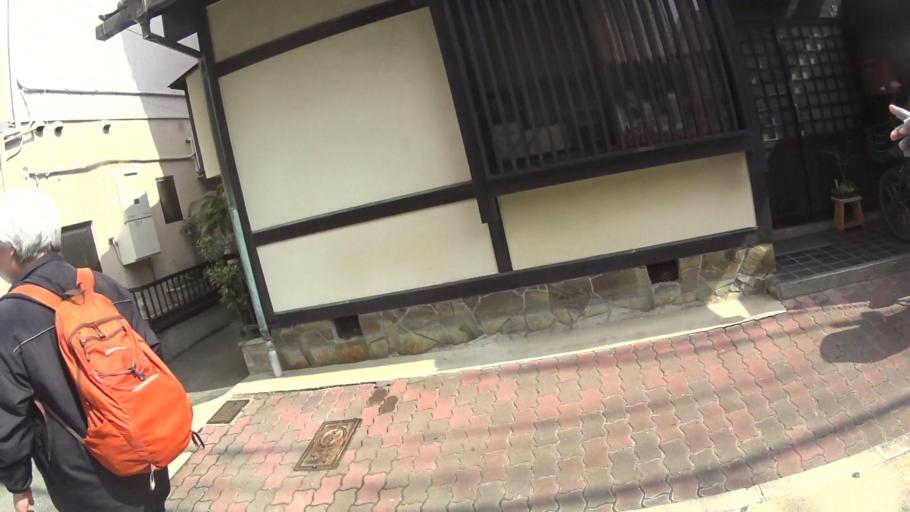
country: JP
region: Osaka
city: Sakai
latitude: 34.6088
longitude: 135.4952
